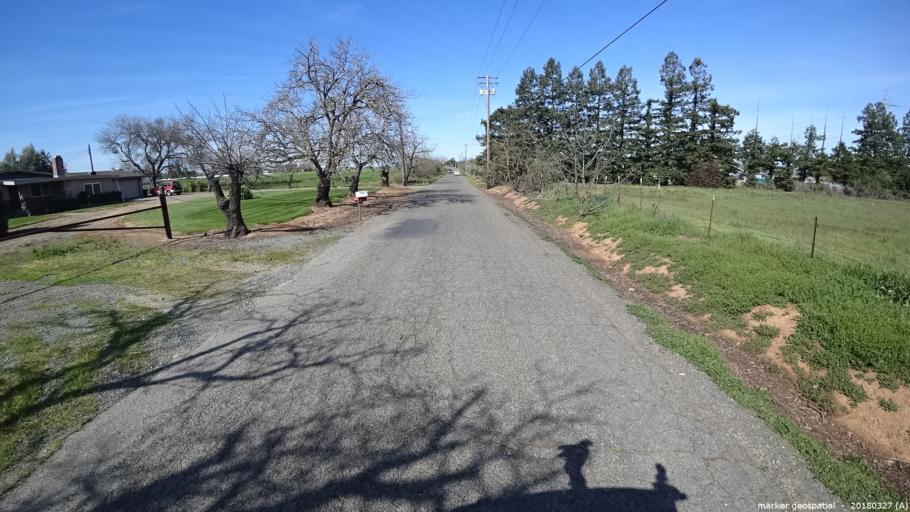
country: US
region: California
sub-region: Sacramento County
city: Vineyard
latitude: 38.5072
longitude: -121.3576
